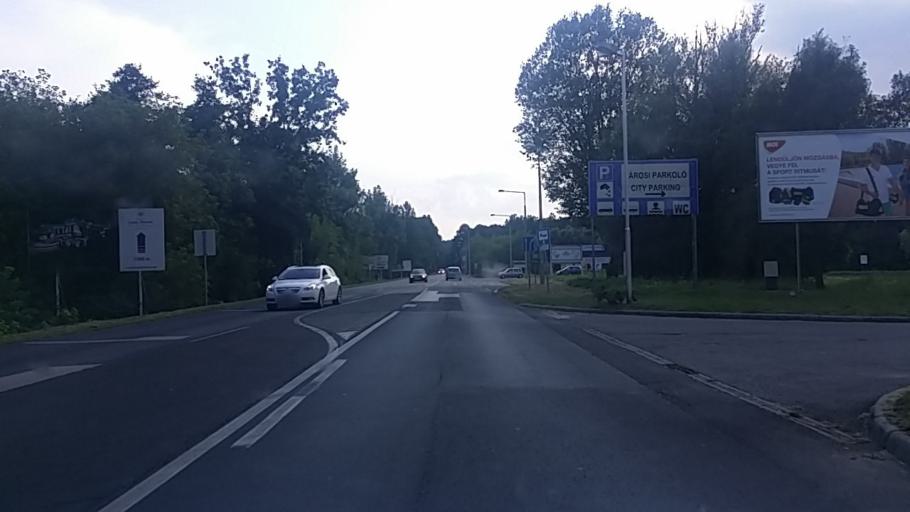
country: HU
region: Zala
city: Heviz
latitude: 46.7915
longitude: 17.2010
